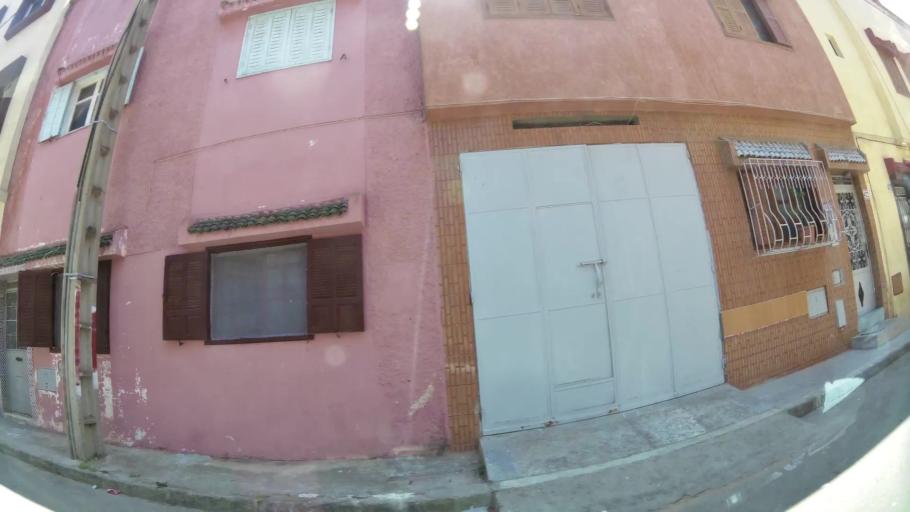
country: MA
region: Gharb-Chrarda-Beni Hssen
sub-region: Kenitra Province
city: Kenitra
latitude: 34.2648
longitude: -6.5546
